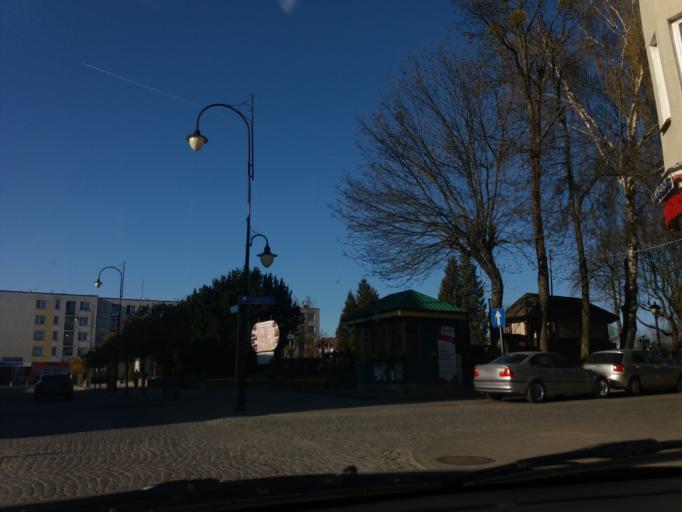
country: PL
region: Warmian-Masurian Voivodeship
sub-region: Powiat nidzicki
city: Nidzica
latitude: 53.3596
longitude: 20.4261
